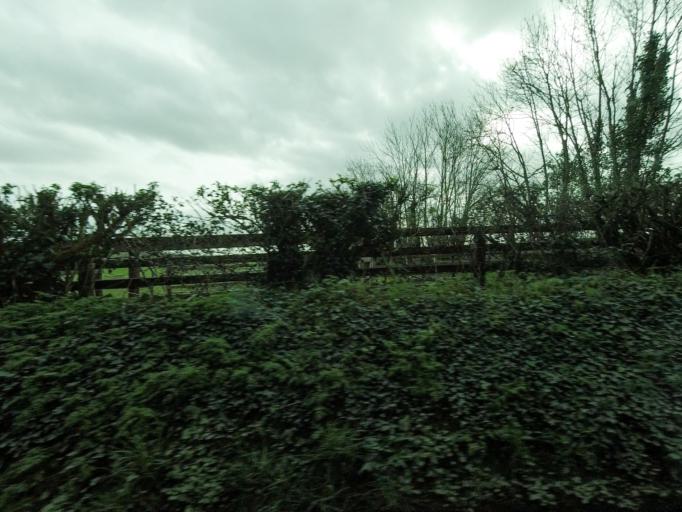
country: IE
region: Leinster
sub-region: Kildare
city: Eadestown
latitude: 53.1729
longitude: -6.6256
